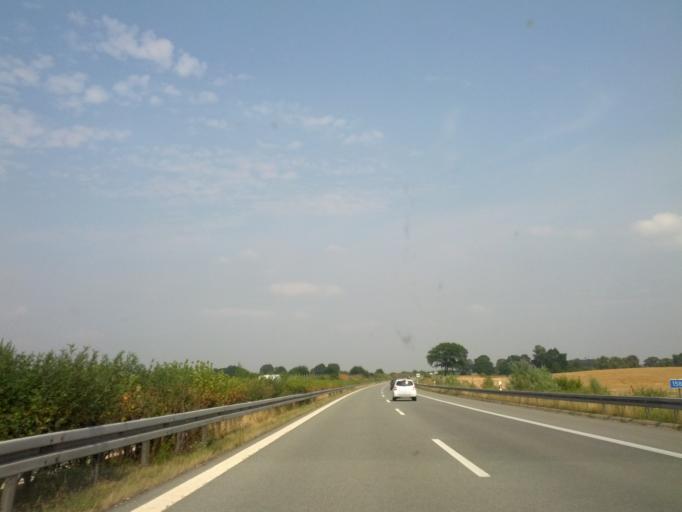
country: DE
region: Mecklenburg-Vorpommern
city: Bad Sulze
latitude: 54.0419
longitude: 12.6102
